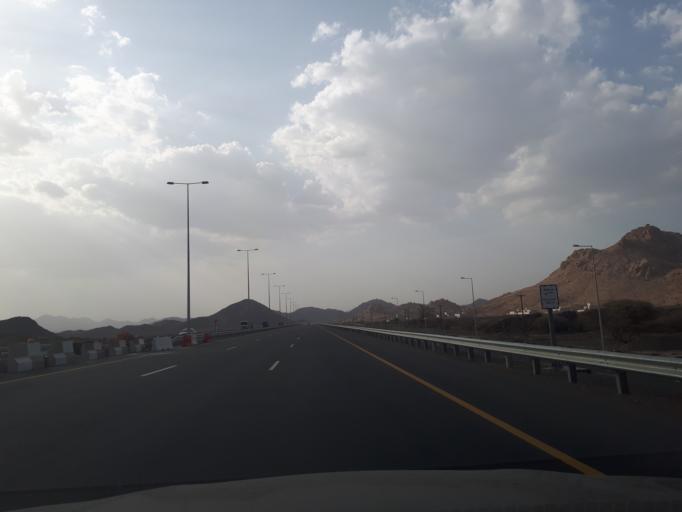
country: OM
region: Ash Sharqiyah
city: Ibra'
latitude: 22.9243
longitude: 58.2620
